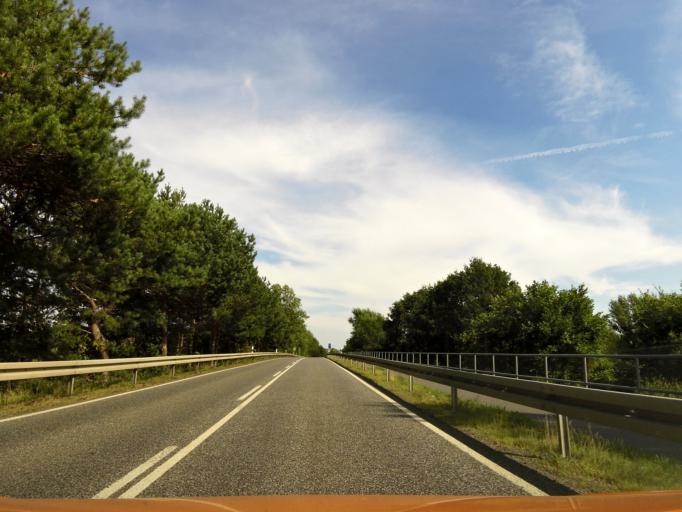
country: DE
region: Brandenburg
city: Ludwigsfelde
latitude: 52.3195
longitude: 13.1987
